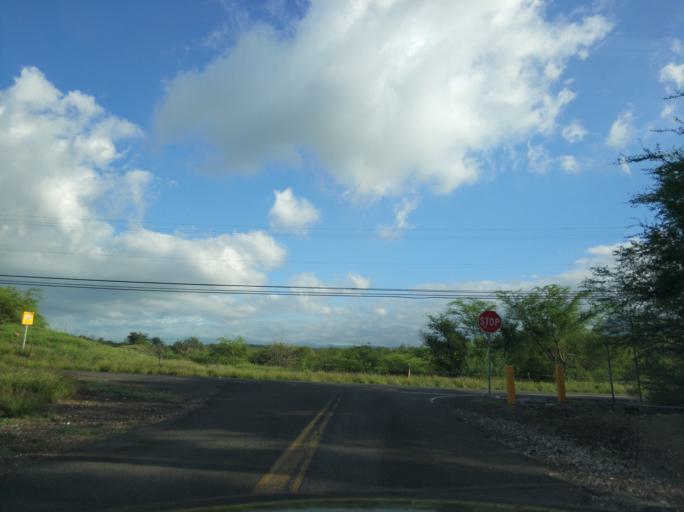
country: US
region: Hawaii
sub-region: Hawaii County
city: Waikoloa Village
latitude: 19.9734
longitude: -155.8307
